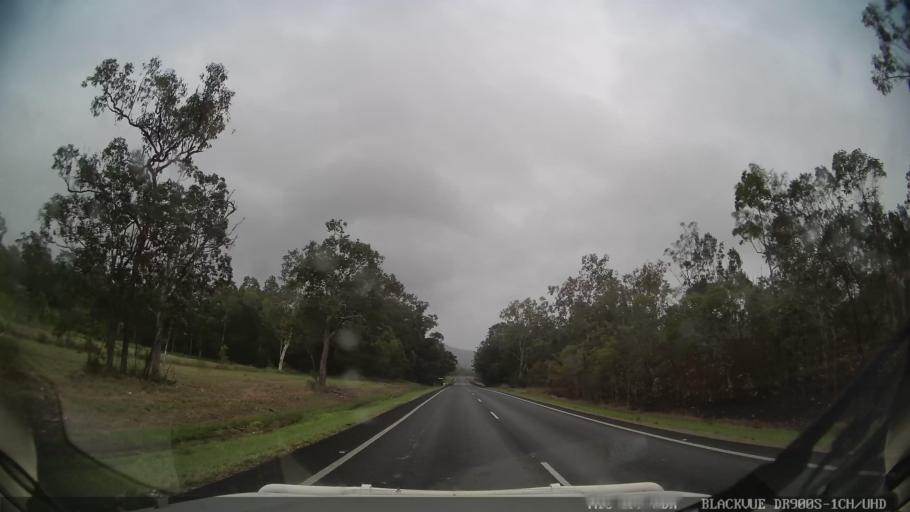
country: AU
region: Queensland
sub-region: Hinchinbrook
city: Ingham
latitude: -18.4427
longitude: 146.1402
